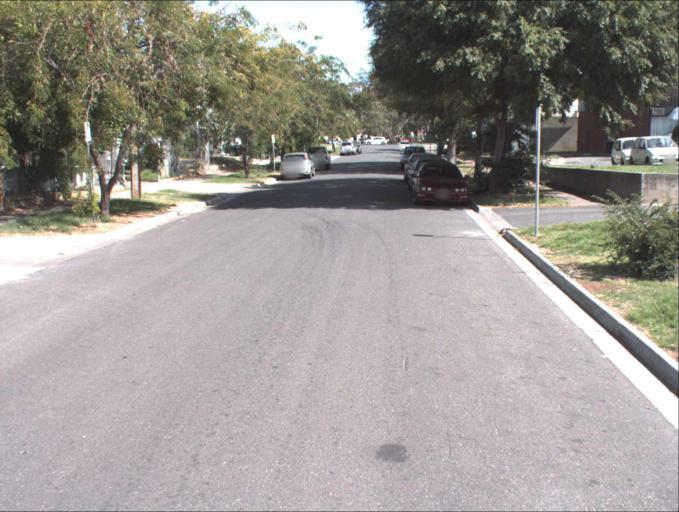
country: AU
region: South Australia
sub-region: Port Adelaide Enfield
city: Gilles Plains
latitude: -34.8625
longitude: 138.6511
